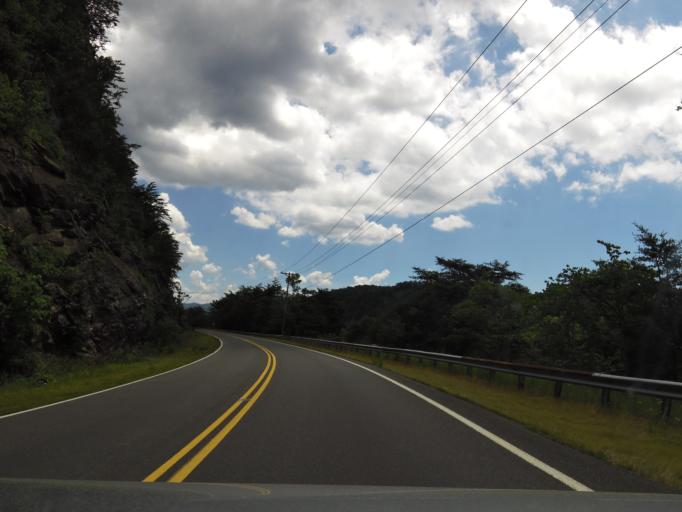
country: US
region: Tennessee
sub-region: Loudon County
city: Greenback
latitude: 35.5433
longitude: -84.0419
